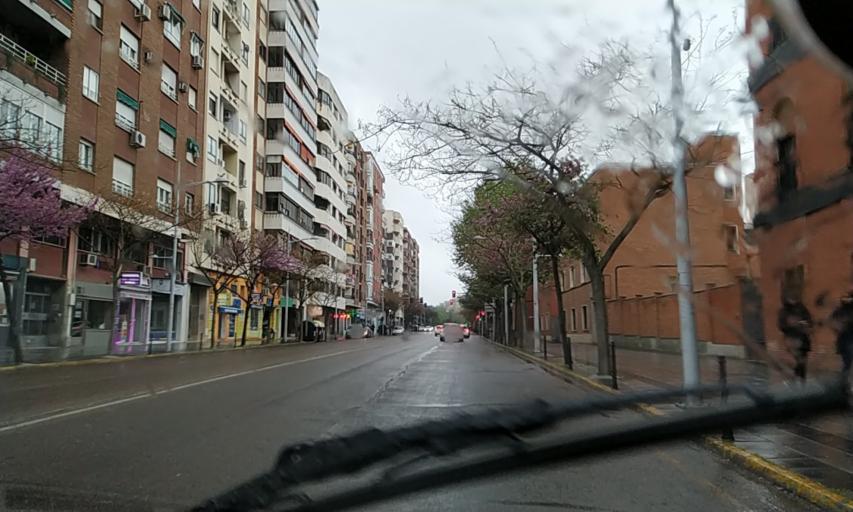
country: ES
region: Extremadura
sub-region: Provincia de Badajoz
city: Badajoz
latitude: 38.8721
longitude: -6.9729
